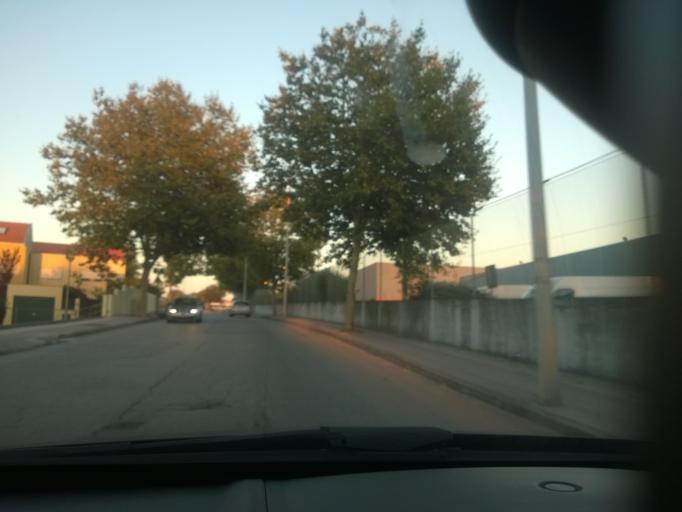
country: PT
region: Porto
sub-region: Matosinhos
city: Santa Cruz do Bispo
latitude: 41.2224
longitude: -8.7028
